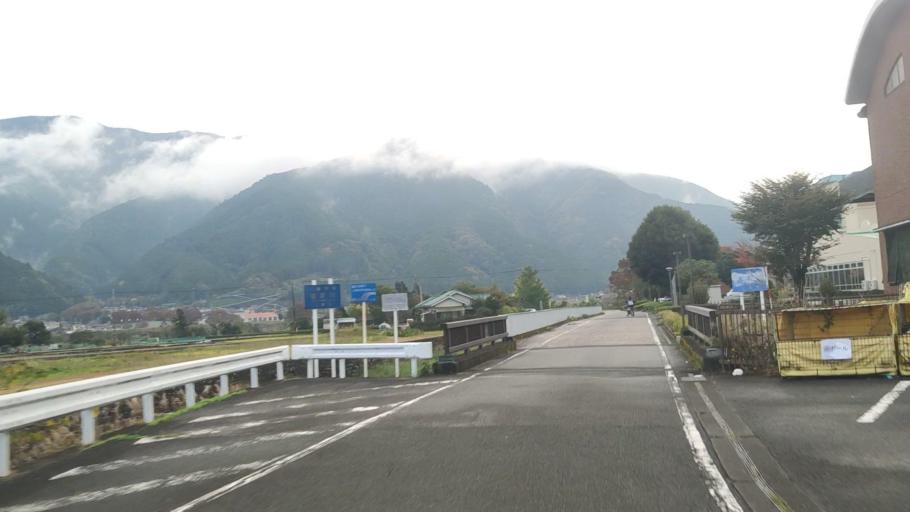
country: JP
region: Shizuoka
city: Fujinomiya
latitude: 35.2800
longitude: 138.4554
